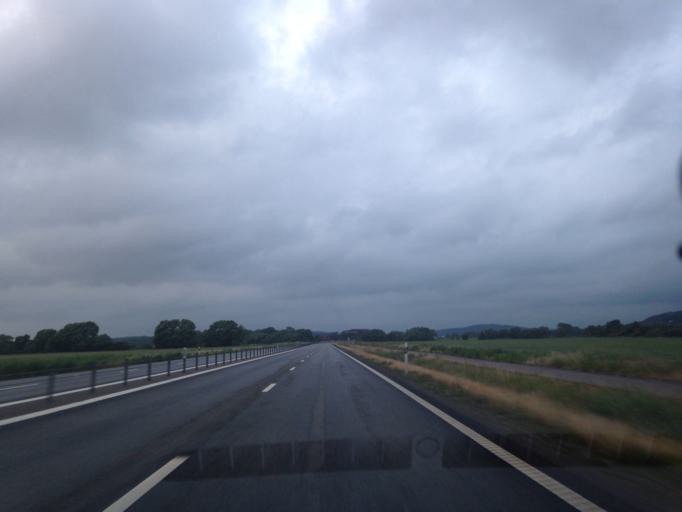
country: SE
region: Halland
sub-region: Varbergs Kommun
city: Varberg
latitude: 57.1352
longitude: 12.2630
